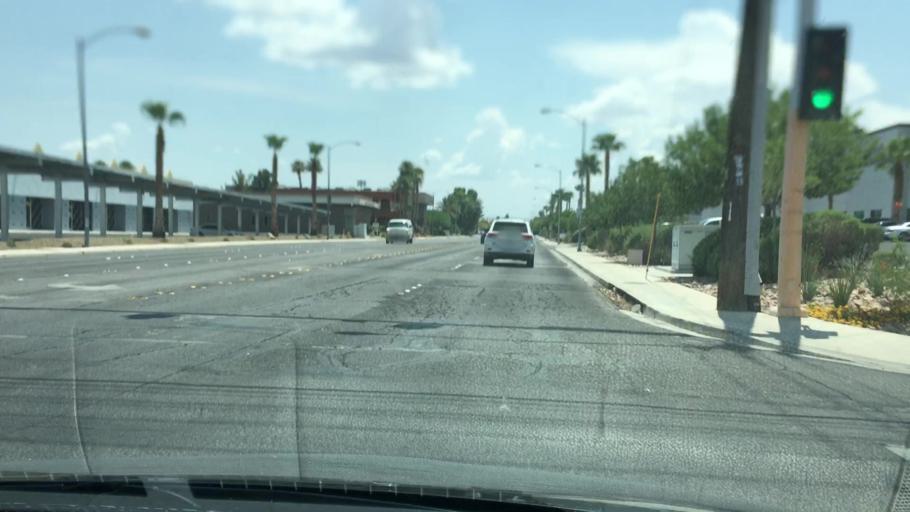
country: US
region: Nevada
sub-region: Clark County
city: Whitney
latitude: 36.0786
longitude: -115.0916
